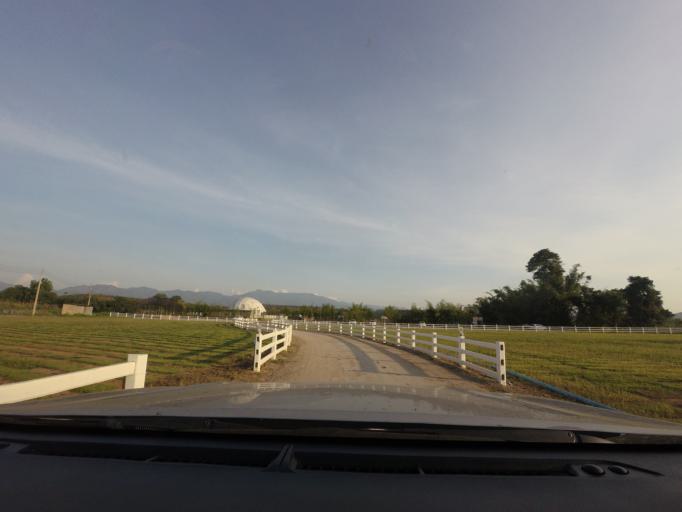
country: TH
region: Chiang Mai
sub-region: Amphoe Chiang Dao
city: Chiang Dao
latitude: 19.3345
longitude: 98.9613
